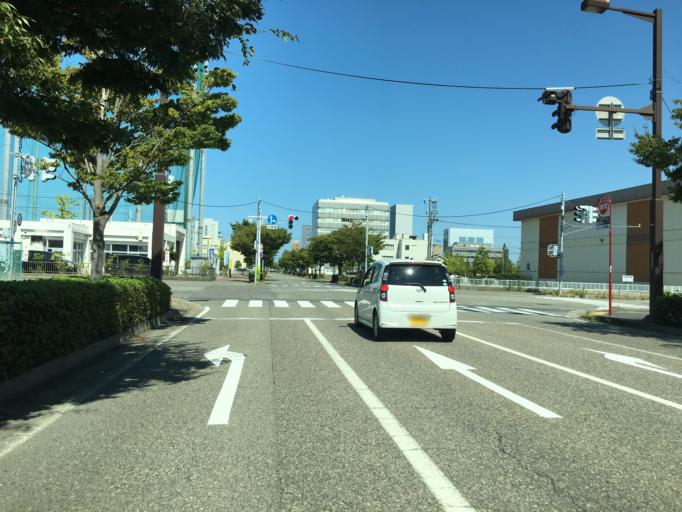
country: JP
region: Niigata
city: Niigata-shi
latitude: 37.8960
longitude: 139.0178
